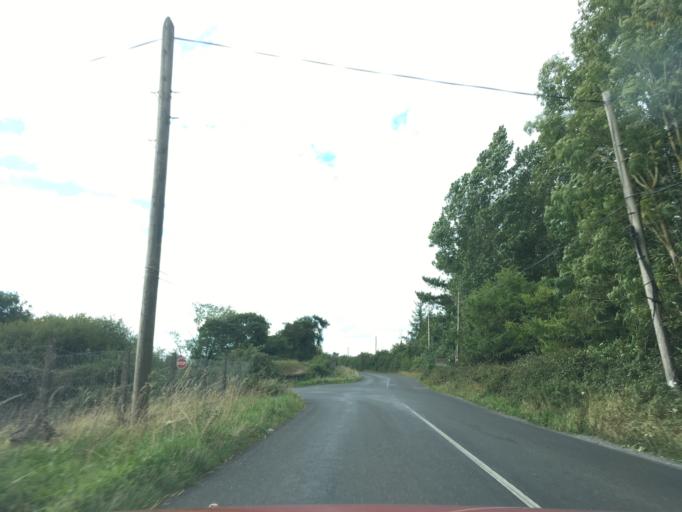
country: IE
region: Munster
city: Cashel
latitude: 52.4574
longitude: -7.9167
